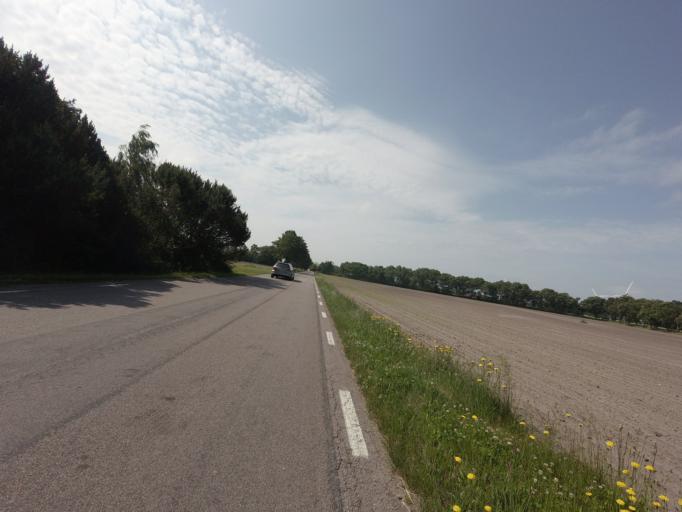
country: SE
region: Skane
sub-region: Helsingborg
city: Odakra
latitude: 56.2056
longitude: 12.7049
